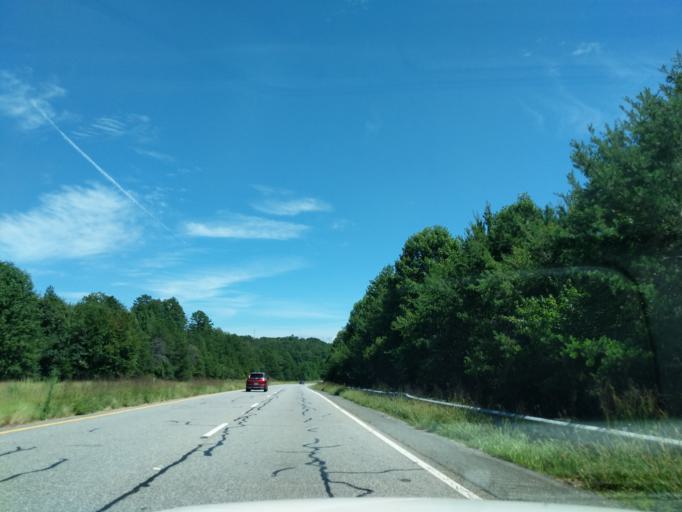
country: US
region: Georgia
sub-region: Fannin County
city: Blue Ridge
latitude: 34.8892
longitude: -84.2151
